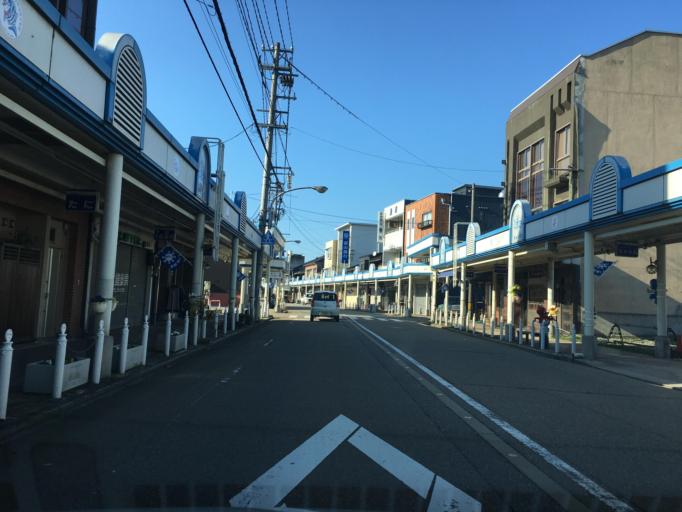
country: JP
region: Toyama
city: Himi
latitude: 36.8576
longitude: 136.9874
